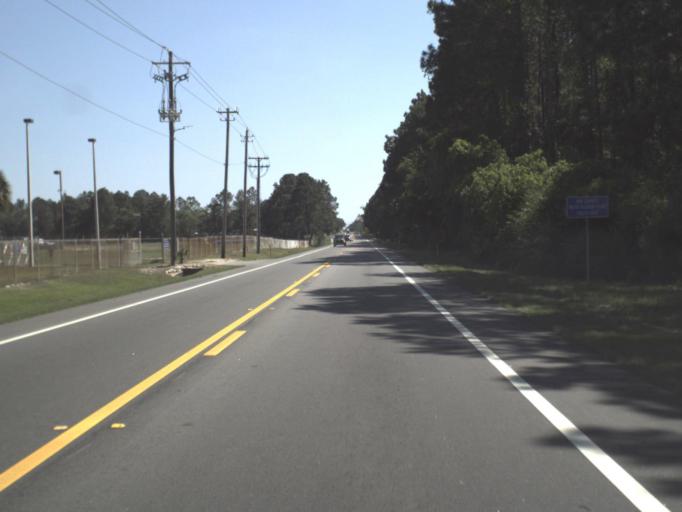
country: US
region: Florida
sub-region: Bay County
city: Hiland Park
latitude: 30.2099
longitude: -85.6077
